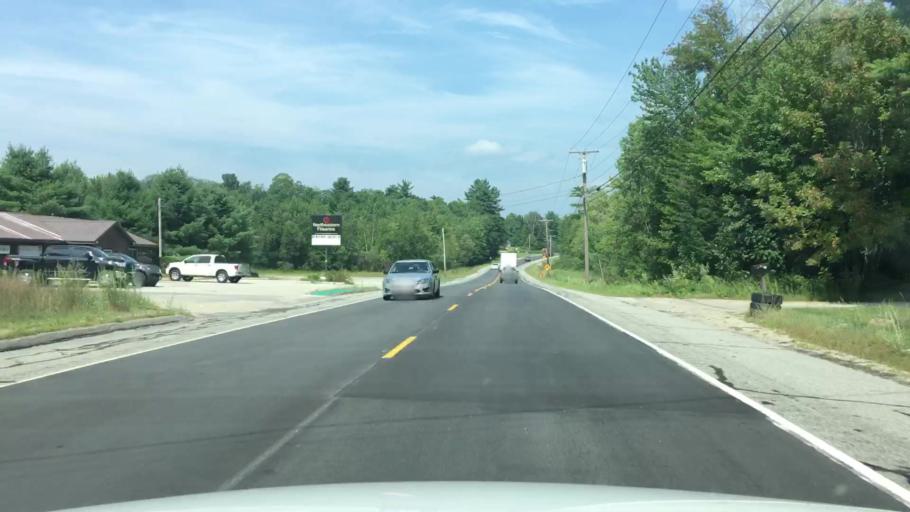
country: US
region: Maine
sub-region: Androscoggin County
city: Turner
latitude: 44.2387
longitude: -70.2586
